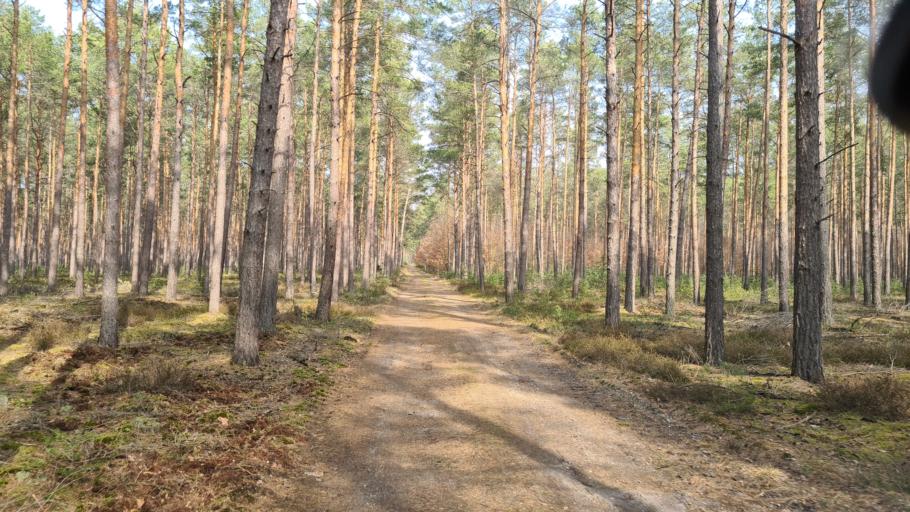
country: DE
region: Brandenburg
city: Trobitz
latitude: 51.6504
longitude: 13.4580
